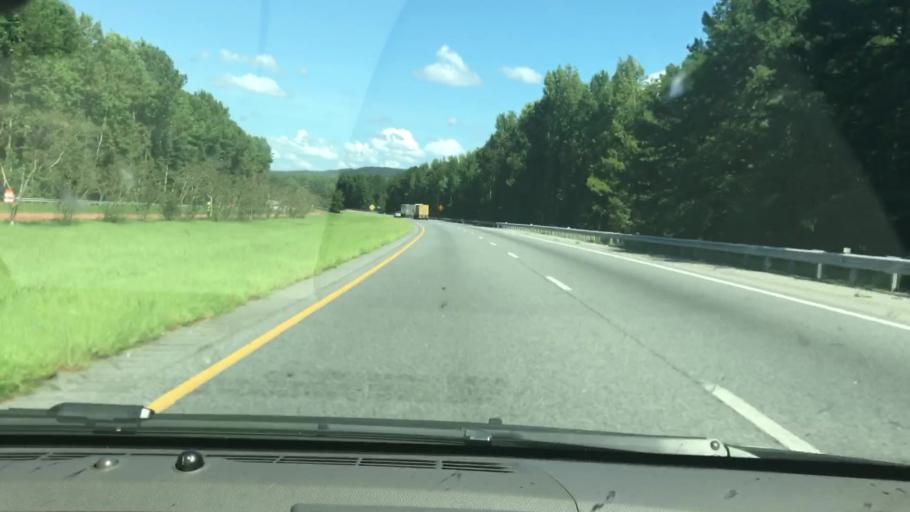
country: US
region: Georgia
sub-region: Harris County
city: Hamilton
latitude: 32.6883
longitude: -84.9912
